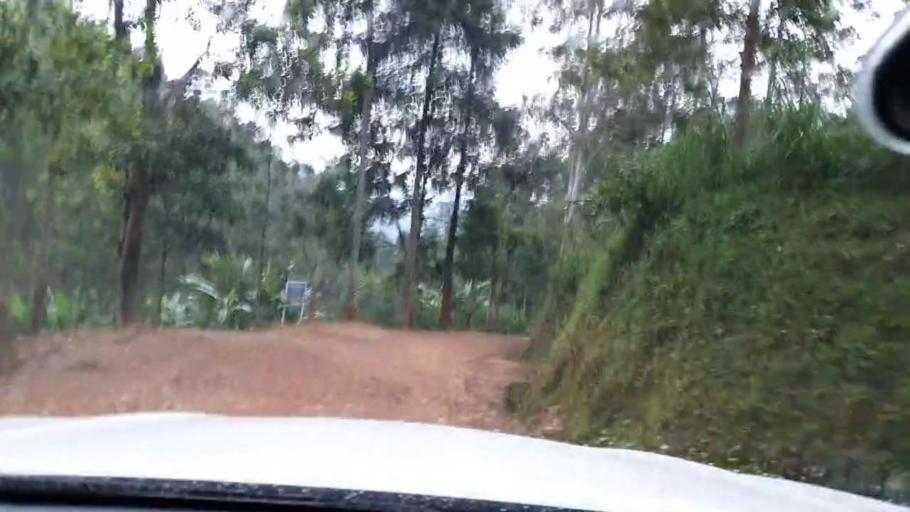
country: RW
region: Western Province
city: Cyangugu
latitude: -2.4086
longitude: 29.2038
